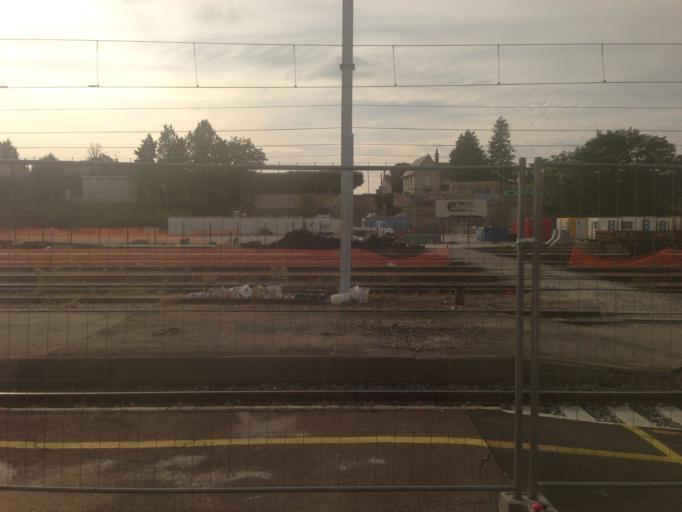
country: FR
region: Centre
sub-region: Departement du Loir-et-Cher
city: Blois
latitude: 47.5869
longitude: 1.3235
